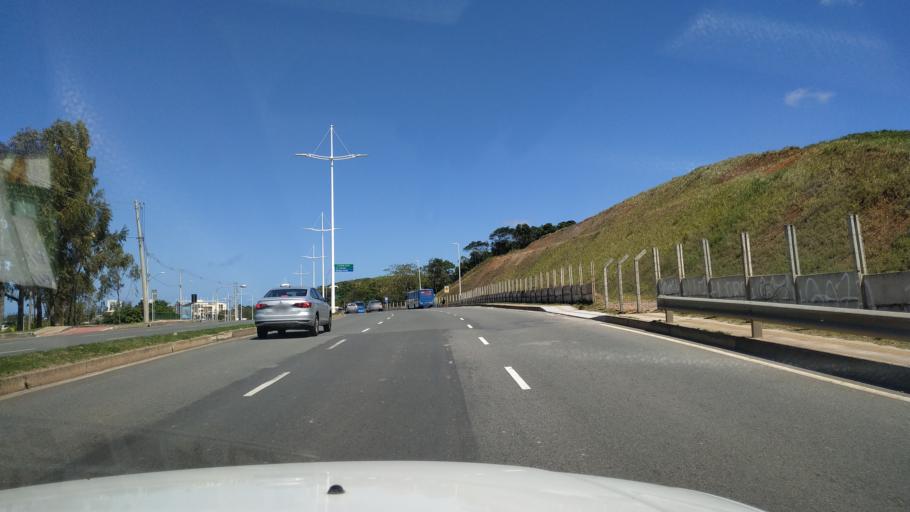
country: BR
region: Bahia
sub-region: Lauro De Freitas
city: Lauro de Freitas
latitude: -12.9329
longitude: -38.3837
